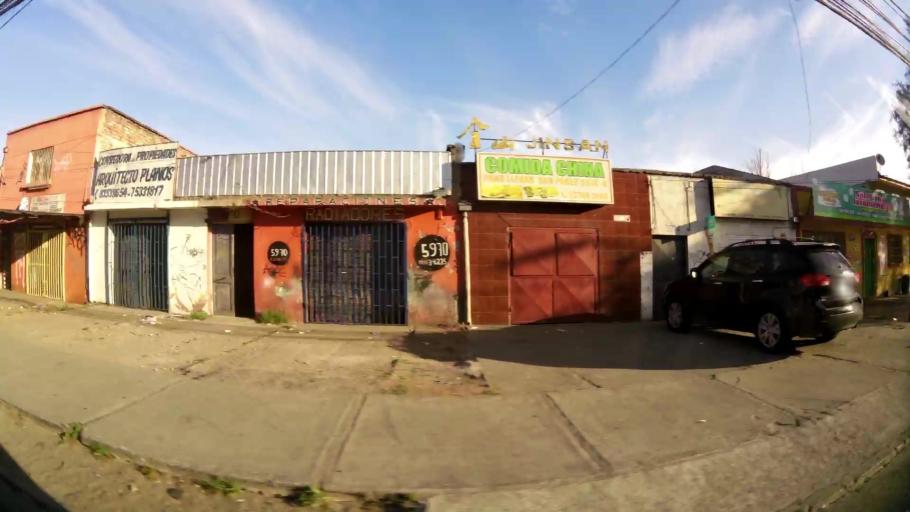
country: CL
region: Santiago Metropolitan
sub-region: Provincia de Santiago
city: Lo Prado
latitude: -33.4438
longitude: -70.7187
